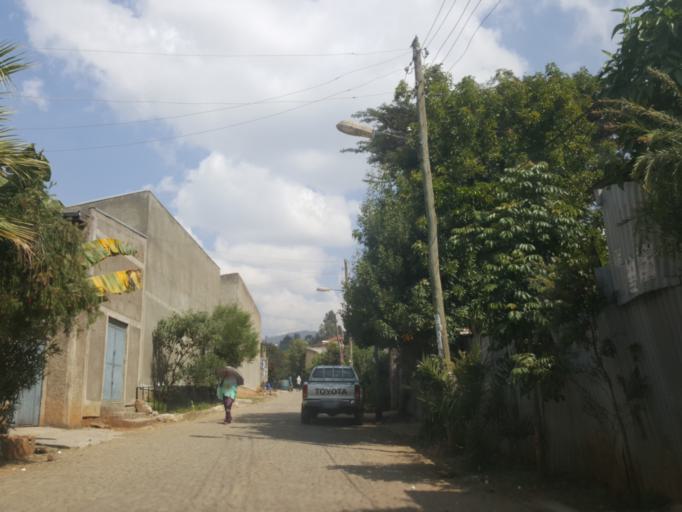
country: ET
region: Adis Abeba
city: Addis Ababa
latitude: 9.0565
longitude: 38.7206
